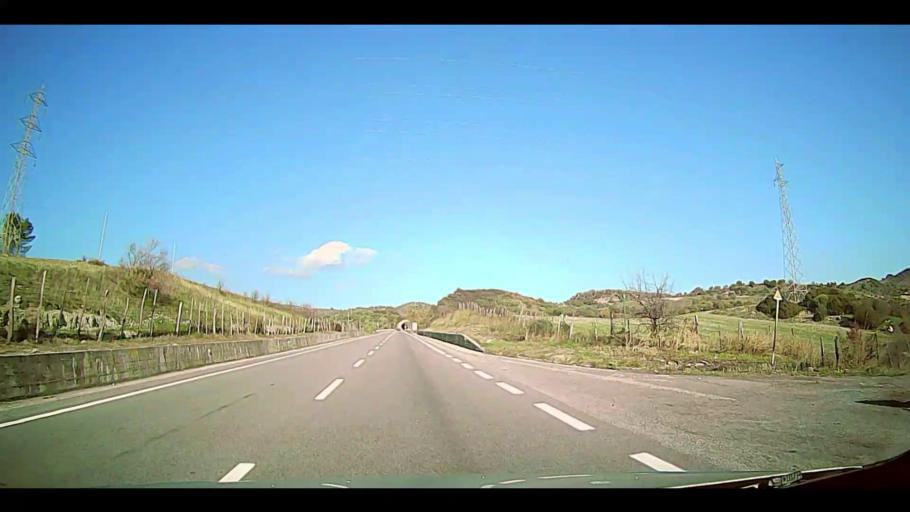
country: IT
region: Calabria
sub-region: Provincia di Crotone
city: Cotronei
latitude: 39.1906
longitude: 16.8155
